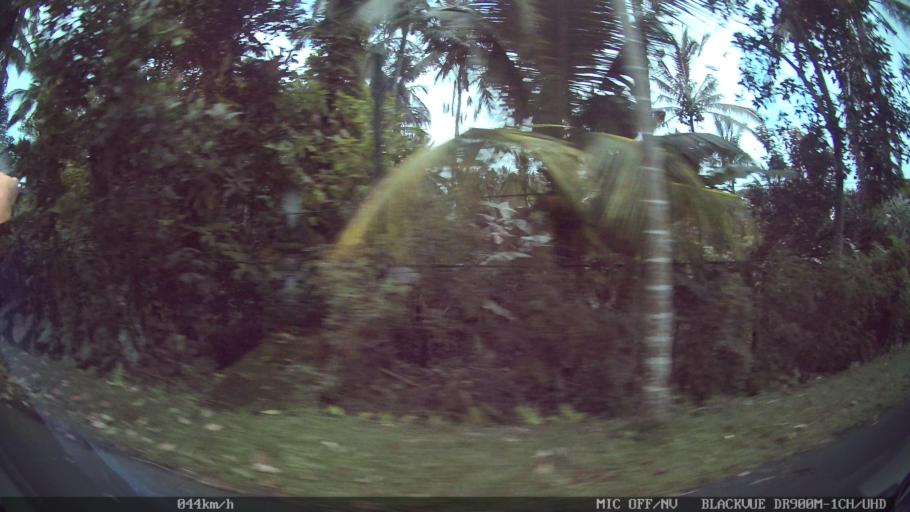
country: ID
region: Bali
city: Badung
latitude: -8.4306
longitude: 115.2260
